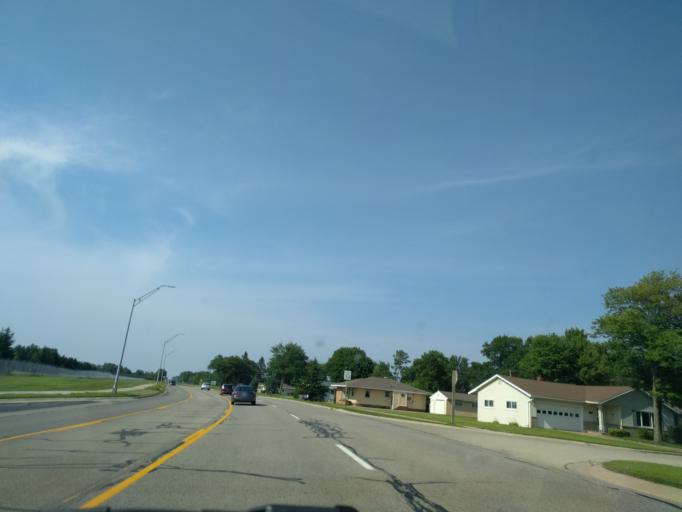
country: US
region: Michigan
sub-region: Delta County
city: Escanaba
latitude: 45.7173
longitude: -87.0803
